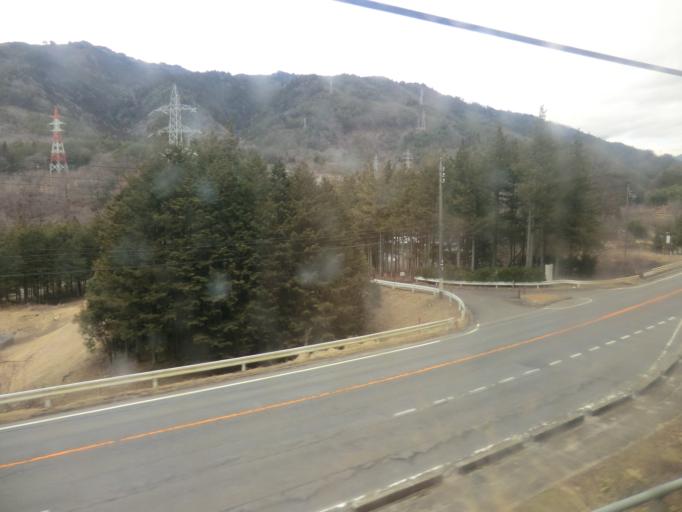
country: JP
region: Nagano
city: Iida
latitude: 35.7045
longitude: 137.7008
